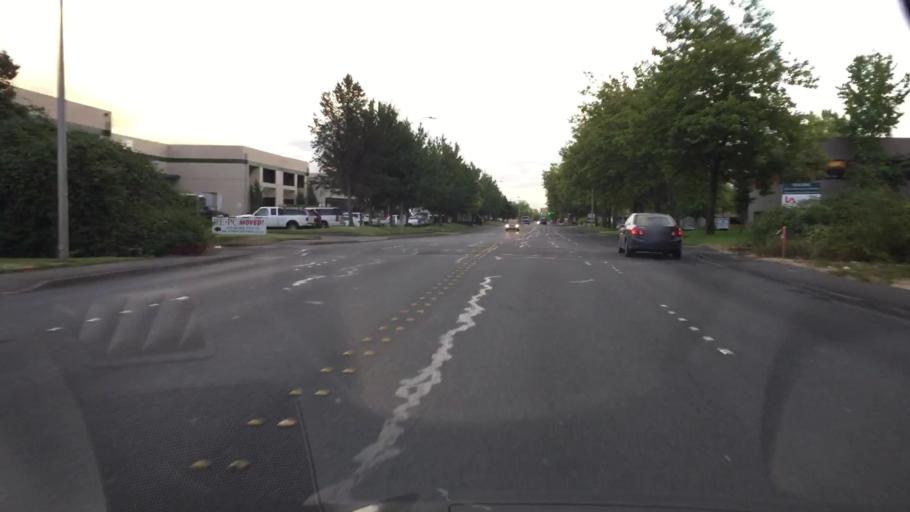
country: US
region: Washington
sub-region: King County
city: Tukwila
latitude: 47.4524
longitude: -122.2544
